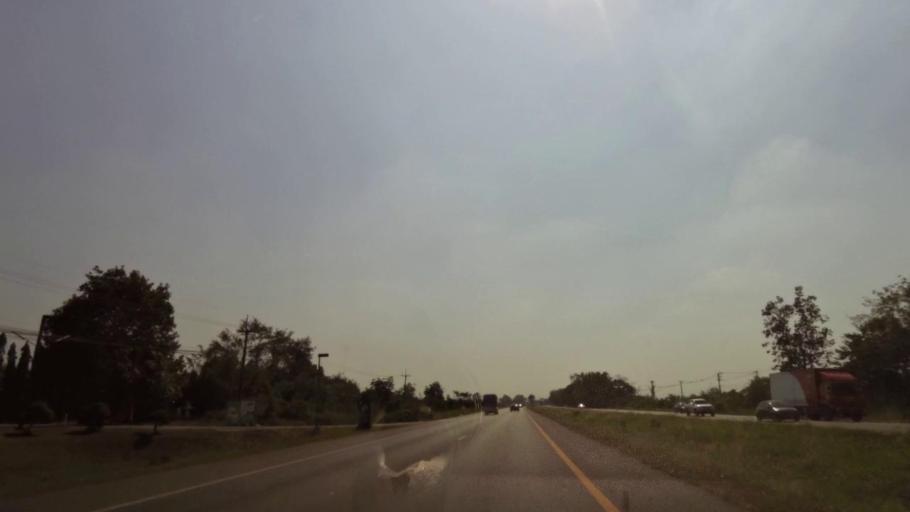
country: TH
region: Phichit
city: Wachira Barami
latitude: 16.4775
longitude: 100.1471
